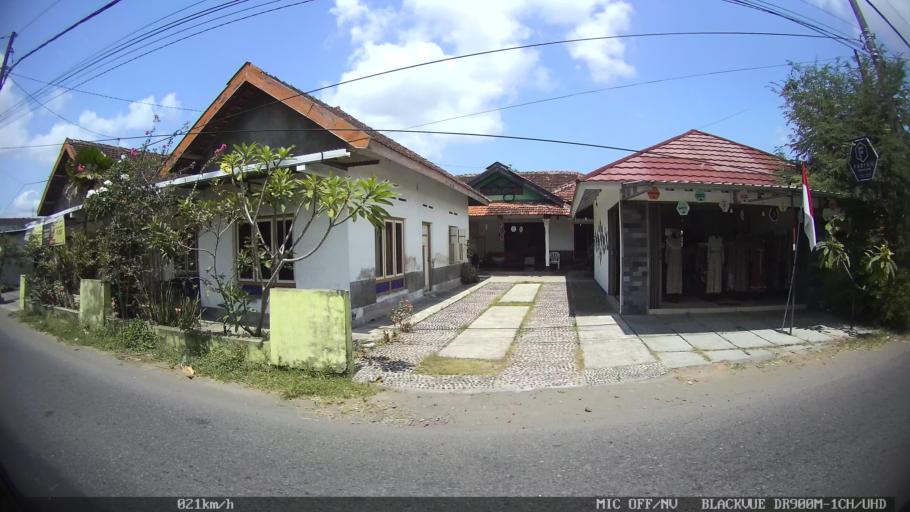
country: ID
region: Daerah Istimewa Yogyakarta
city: Sewon
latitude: -7.8948
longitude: 110.3489
